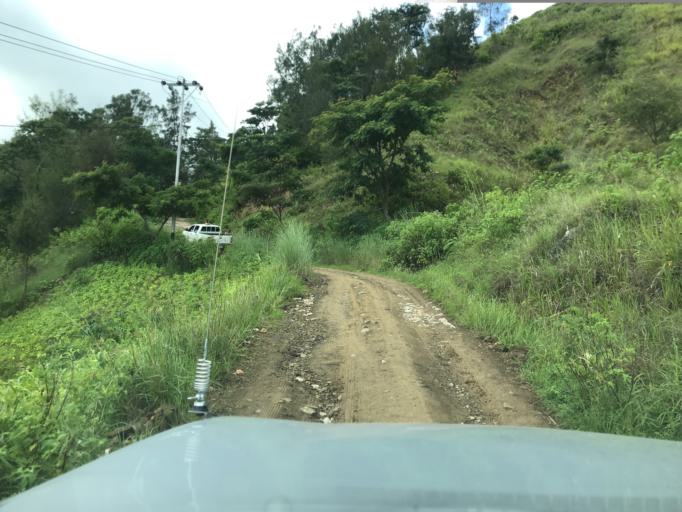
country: TL
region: Aileu
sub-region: Aileu Villa
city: Aileu
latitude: -8.8573
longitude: 125.5761
